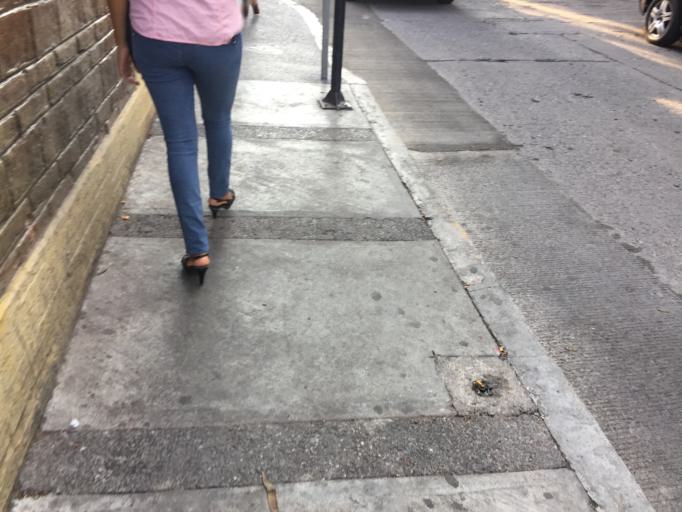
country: MX
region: Guerrero
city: Chilpancingo de los Bravos
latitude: 17.5528
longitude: -99.5004
